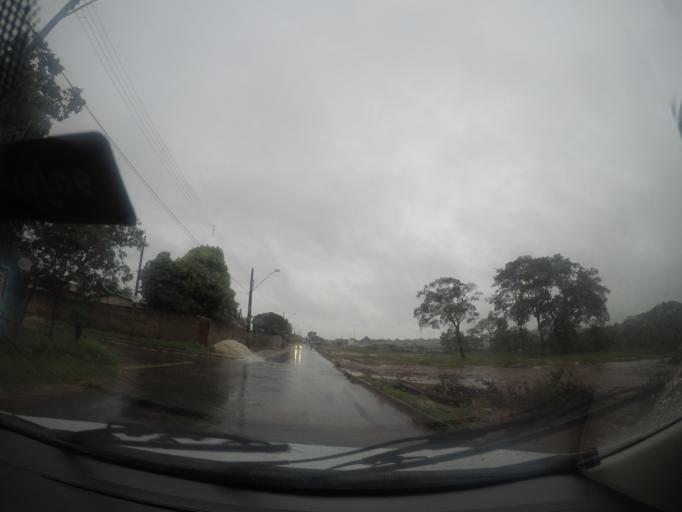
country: BR
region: Goias
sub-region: Goiania
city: Goiania
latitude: -16.6049
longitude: -49.3484
